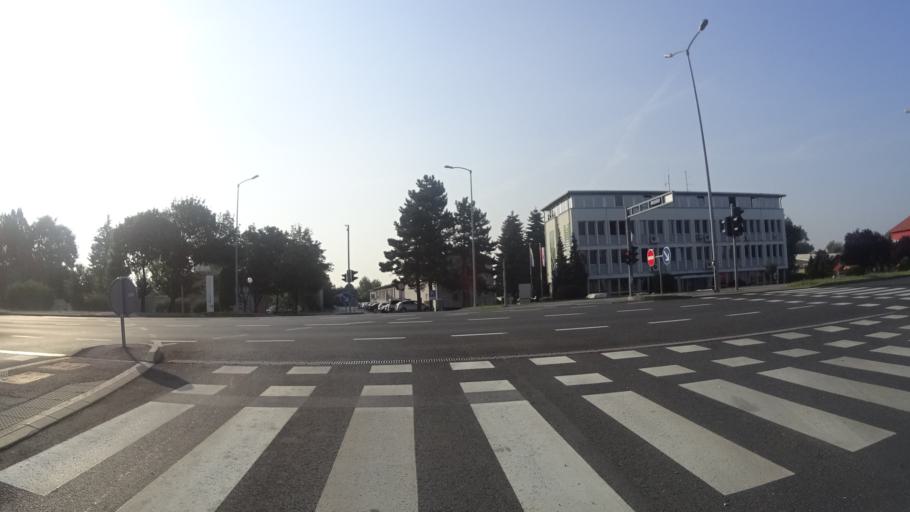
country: HR
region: Varazdinska
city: Varazdin
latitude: 46.3146
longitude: 16.3508
